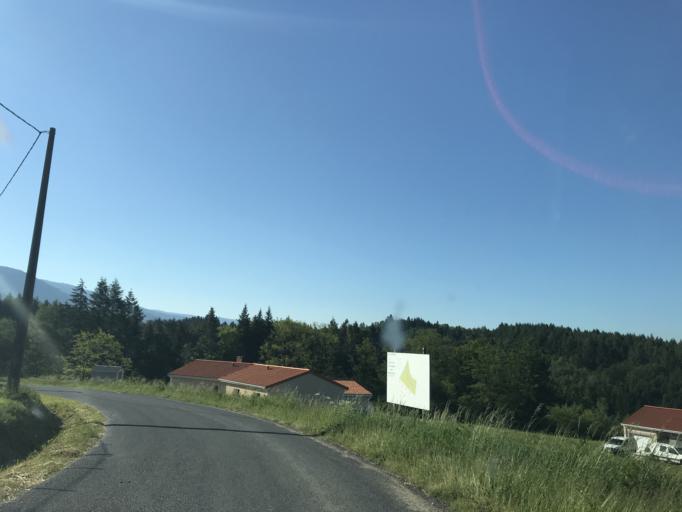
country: FR
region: Auvergne
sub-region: Departement du Puy-de-Dome
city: Job
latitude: 45.6620
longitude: 3.6880
